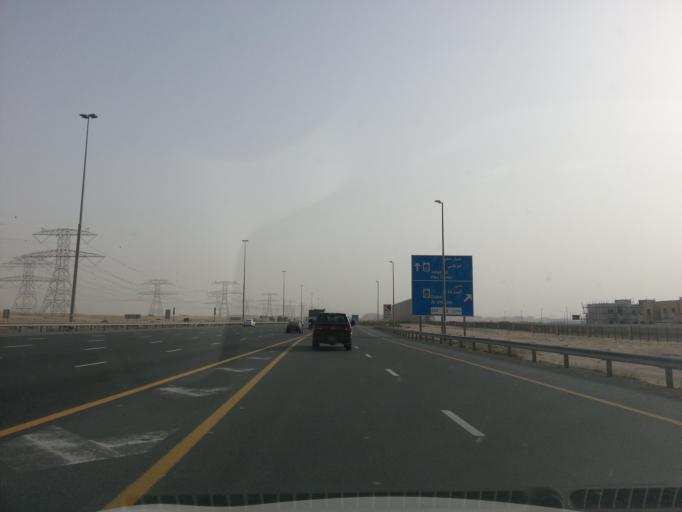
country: AE
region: Dubai
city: Dubai
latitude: 25.0192
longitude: 55.2780
